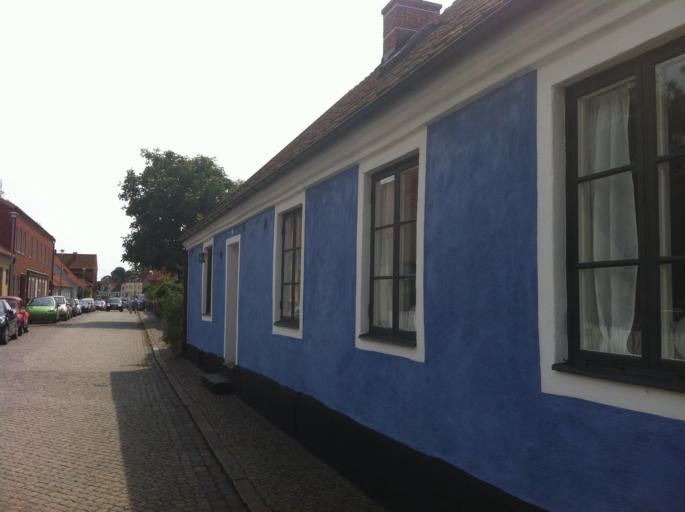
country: SE
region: Skane
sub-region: Simrishamns Kommun
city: Simrishamn
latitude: 55.5587
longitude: 14.3515
